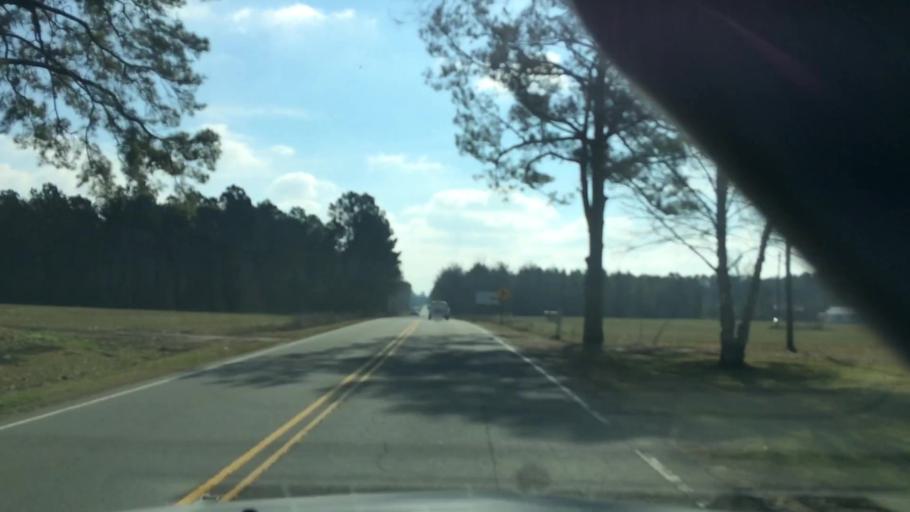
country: US
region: North Carolina
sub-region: Duplin County
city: Beulaville
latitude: 34.8541
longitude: -77.7979
